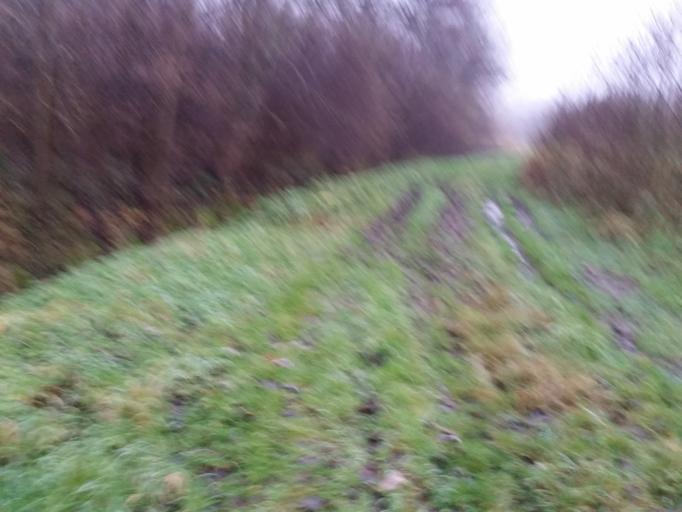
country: BE
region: Flanders
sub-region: Provincie Vlaams-Brabant
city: Zemst
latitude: 50.9456
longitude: 4.4755
